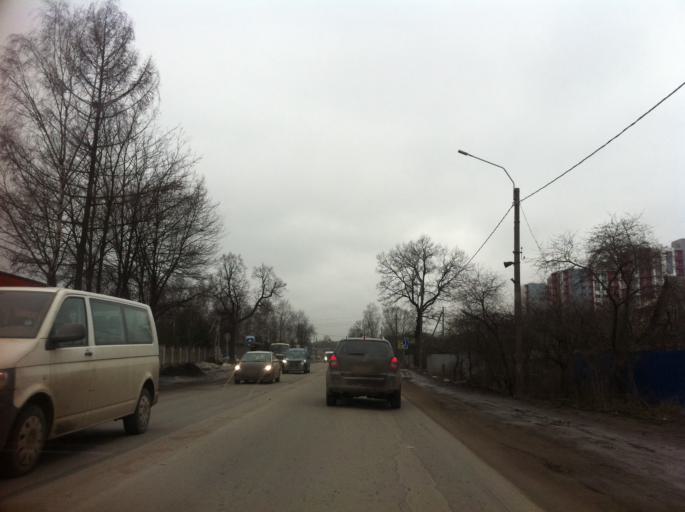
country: RU
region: Leningrad
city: Yanino Vtoroye
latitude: 59.9465
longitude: 30.5671
